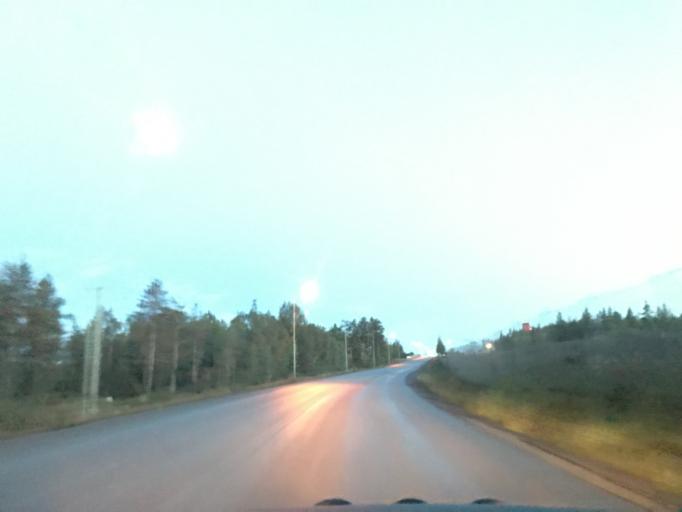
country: SE
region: Norrbotten
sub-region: Gallivare Kommun
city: Malmberget
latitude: 67.6494
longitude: 21.0189
